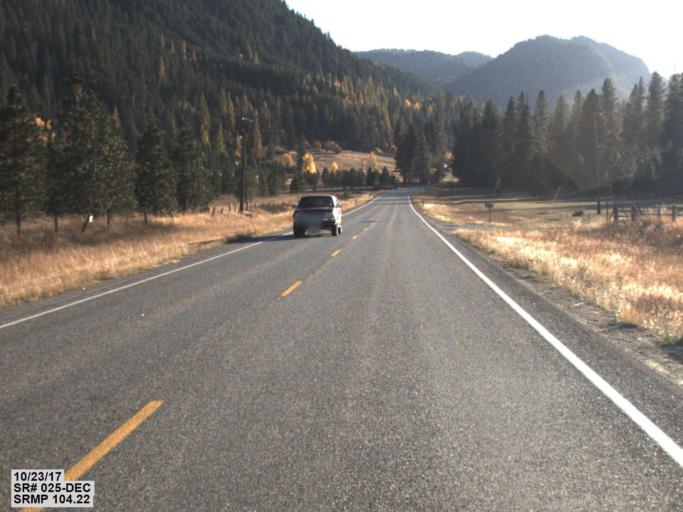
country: US
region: Washington
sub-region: Stevens County
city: Kettle Falls
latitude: 48.8308
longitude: -117.9088
